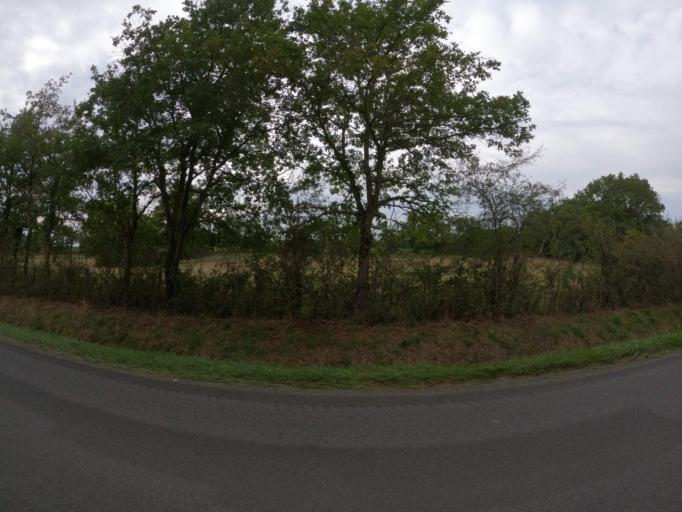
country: FR
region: Poitou-Charentes
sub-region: Departement de la Vienne
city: Saulge
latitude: 46.3588
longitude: 0.8358
